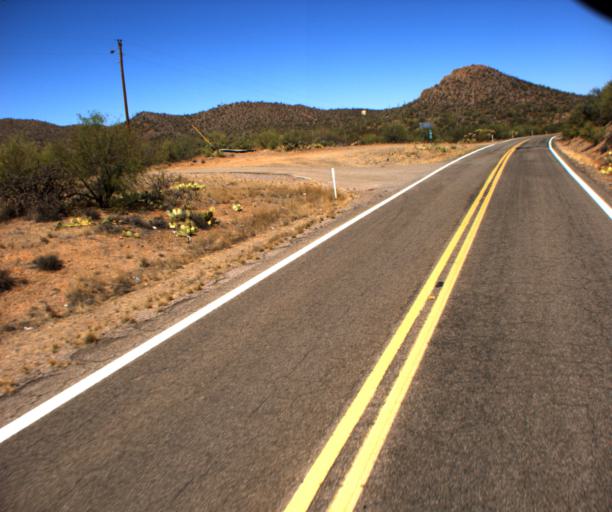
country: US
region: Arizona
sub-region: Pima County
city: Sells
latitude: 32.1702
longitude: -112.1464
